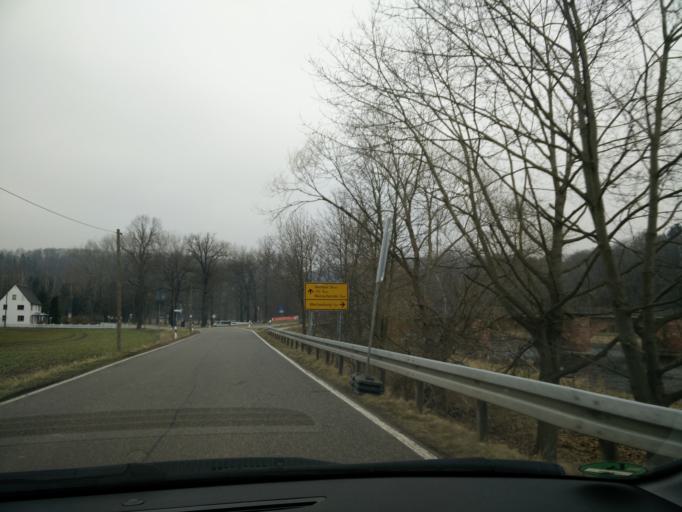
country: DE
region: Saxony
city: Wechselburg
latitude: 51.0023
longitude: 12.7686
